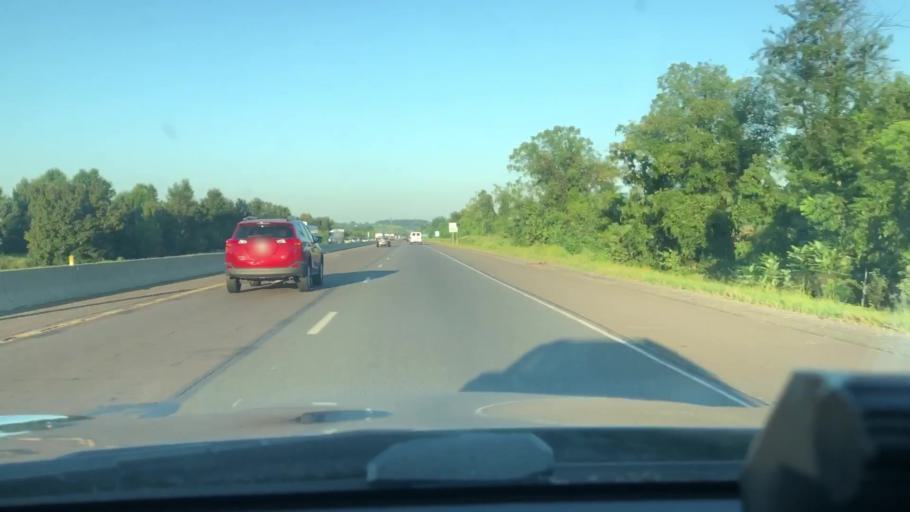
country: US
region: Pennsylvania
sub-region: Lehigh County
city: Breinigsville
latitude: 40.5760
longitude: -75.6342
